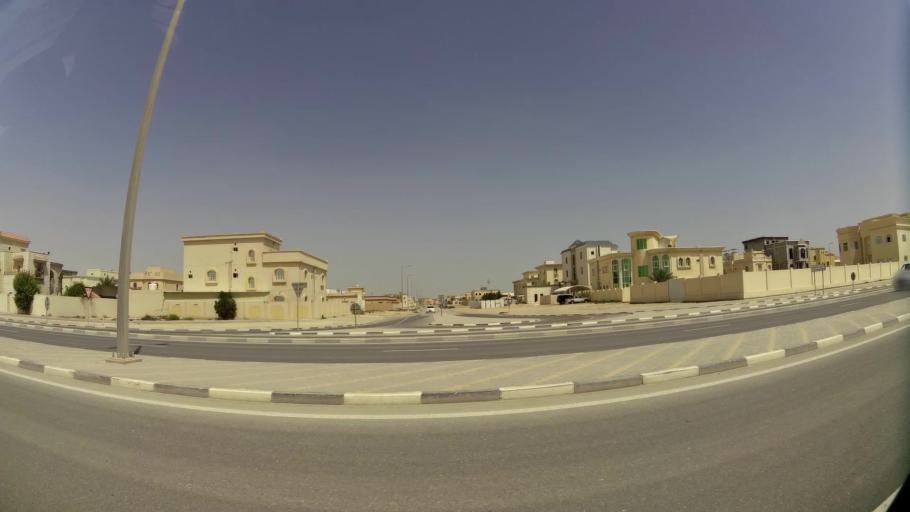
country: QA
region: Baladiyat Umm Salal
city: Umm Salal Muhammad
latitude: 25.3829
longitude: 51.4562
